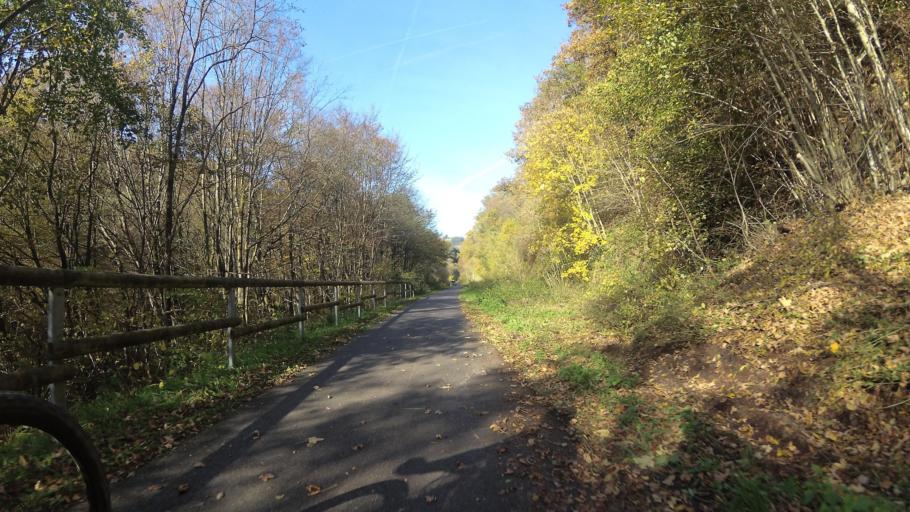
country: DE
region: Rheinland-Pfalz
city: Ollmuth
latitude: 49.6695
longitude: 6.7225
